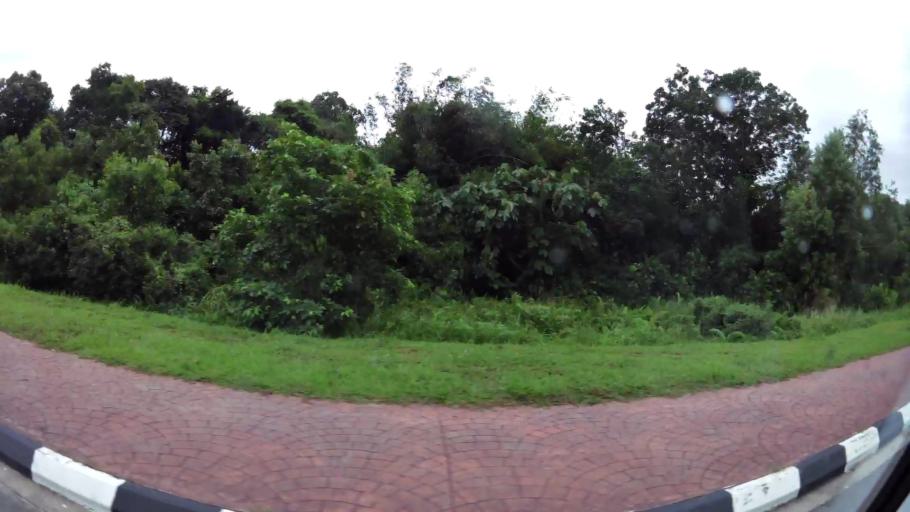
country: BN
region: Brunei and Muara
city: Bandar Seri Begawan
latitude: 4.9010
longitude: 114.9228
